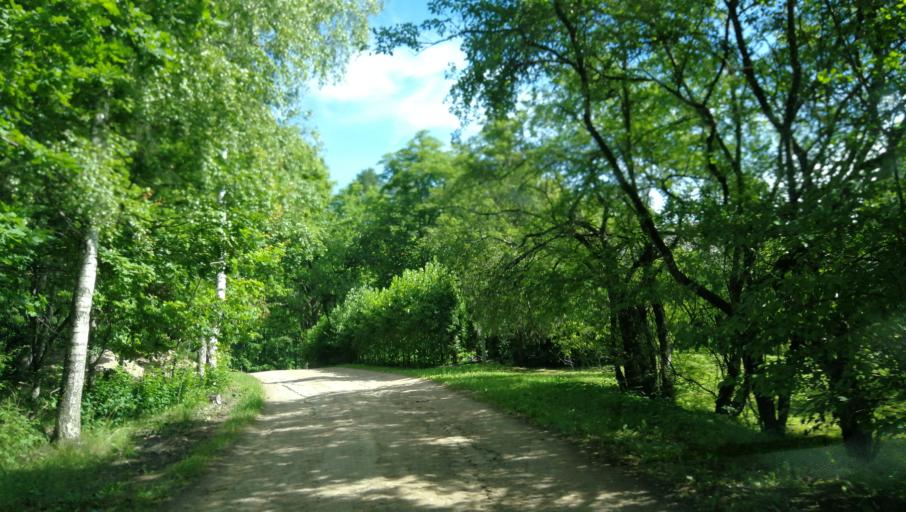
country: LV
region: Gulbenes Rajons
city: Gulbene
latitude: 57.1709
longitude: 26.8656
